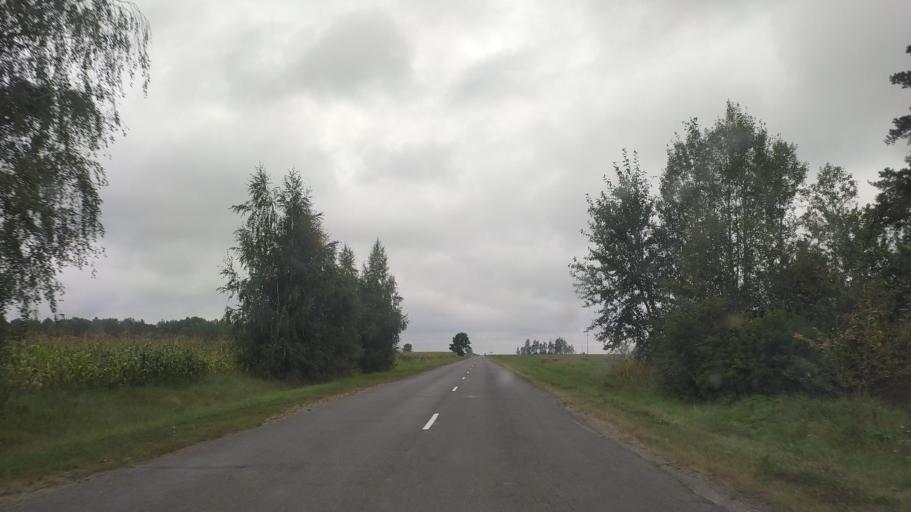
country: BY
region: Brest
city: Byaroza
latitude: 52.5615
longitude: 24.9078
